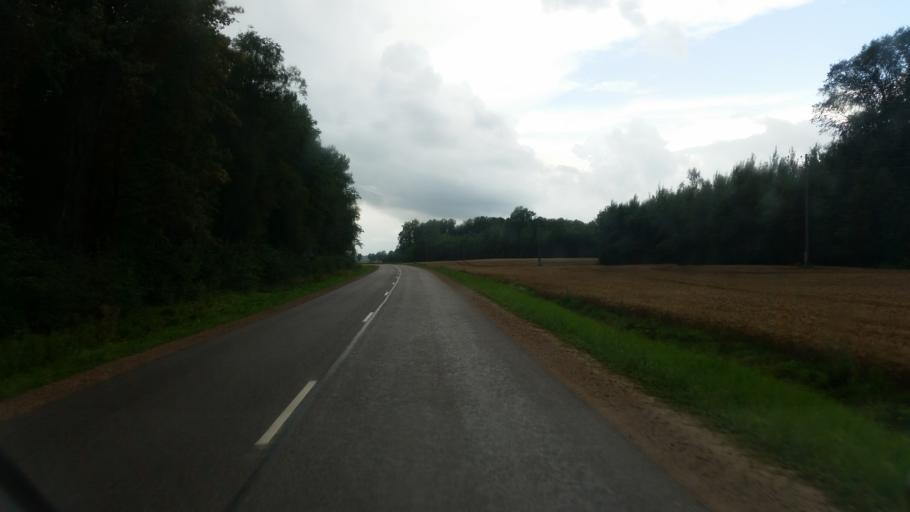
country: LV
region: Vecumnieki
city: Vecumnieki
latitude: 56.4324
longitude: 24.4437
